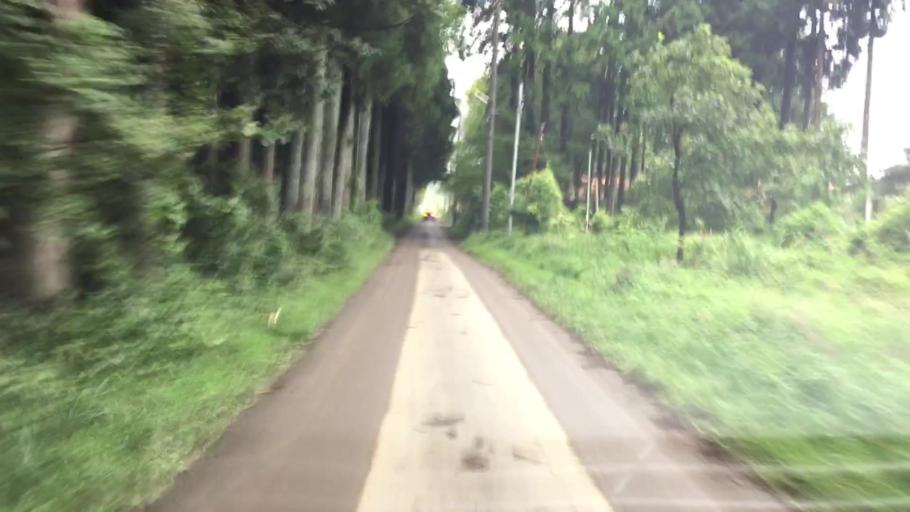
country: JP
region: Yamanashi
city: Fujikawaguchiko
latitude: 35.4017
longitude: 138.5599
